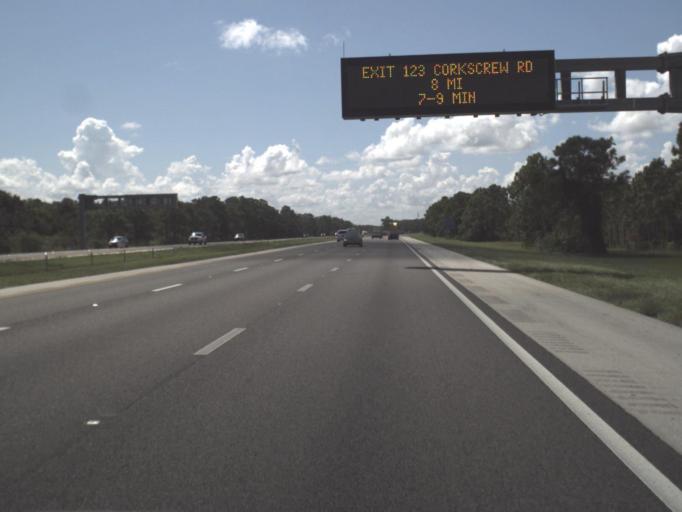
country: US
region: Florida
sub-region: Lee County
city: Gateway
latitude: 26.5904
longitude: -81.7969
